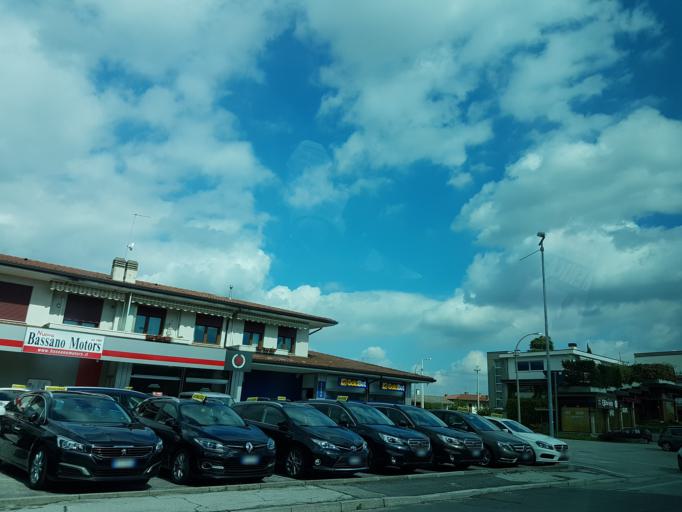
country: IT
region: Veneto
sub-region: Provincia di Vicenza
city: Bassano del Grappa
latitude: 45.7542
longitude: 11.7454
